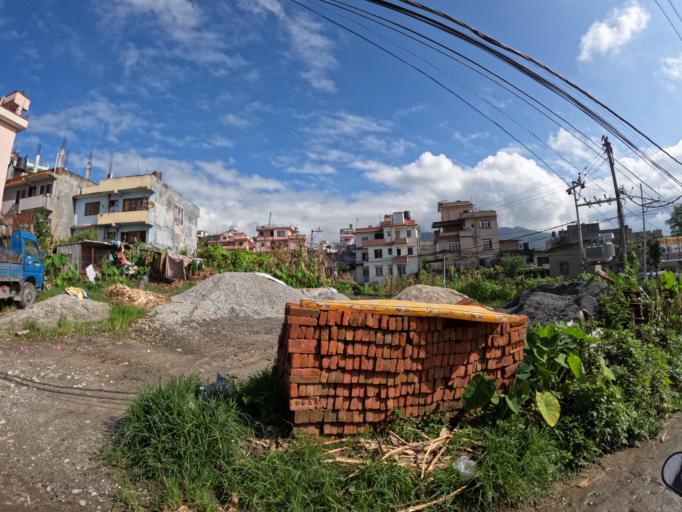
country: NP
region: Central Region
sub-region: Bagmati Zone
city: Kathmandu
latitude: 27.7615
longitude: 85.3314
